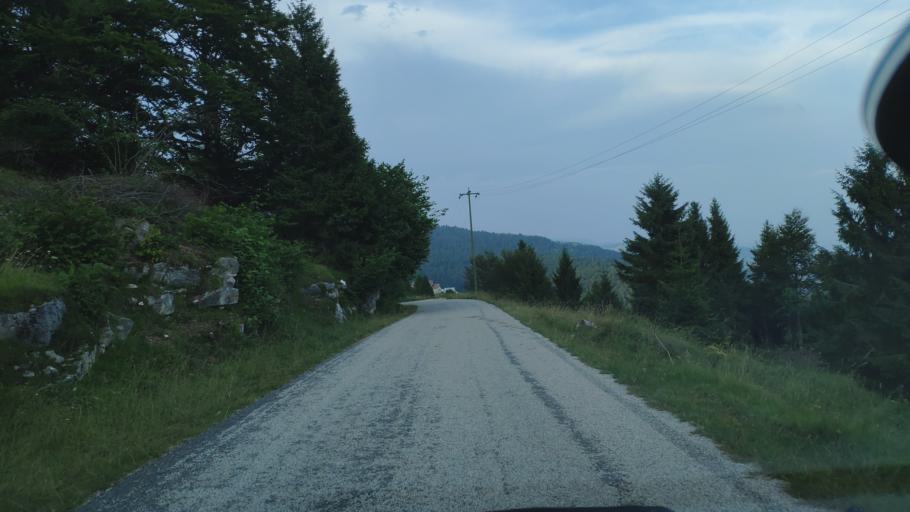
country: IT
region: Veneto
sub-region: Provincia di Vicenza
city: Calvene
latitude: 45.7922
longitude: 11.4903
